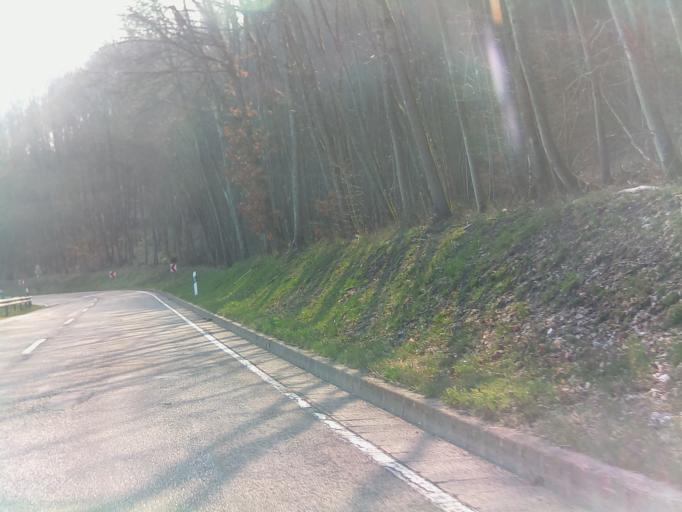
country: DE
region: Rheinland-Pfalz
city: Thallichtenberg
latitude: 49.5754
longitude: 7.3413
